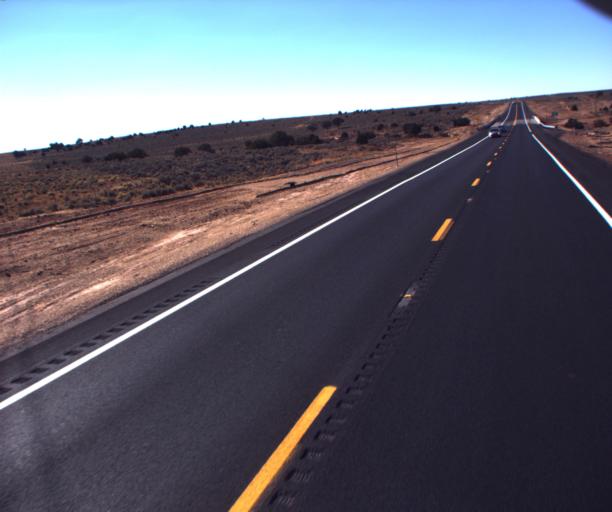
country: US
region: Arizona
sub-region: Apache County
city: Ganado
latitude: 35.7178
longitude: -109.4621
